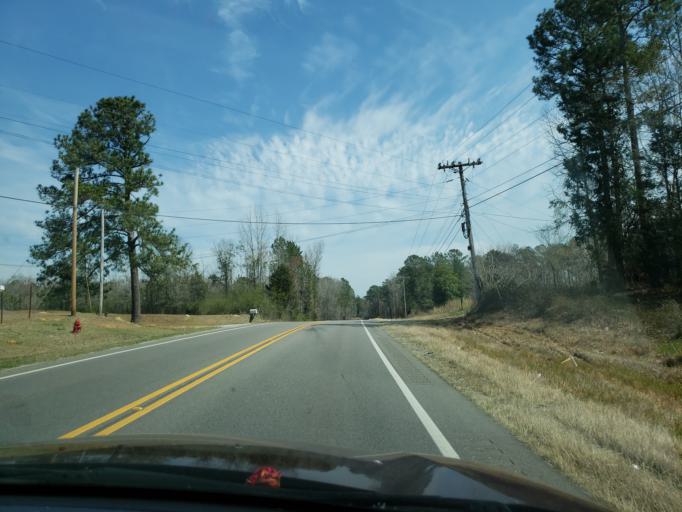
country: US
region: Alabama
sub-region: Elmore County
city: Wetumpka
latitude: 32.5648
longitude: -86.1322
